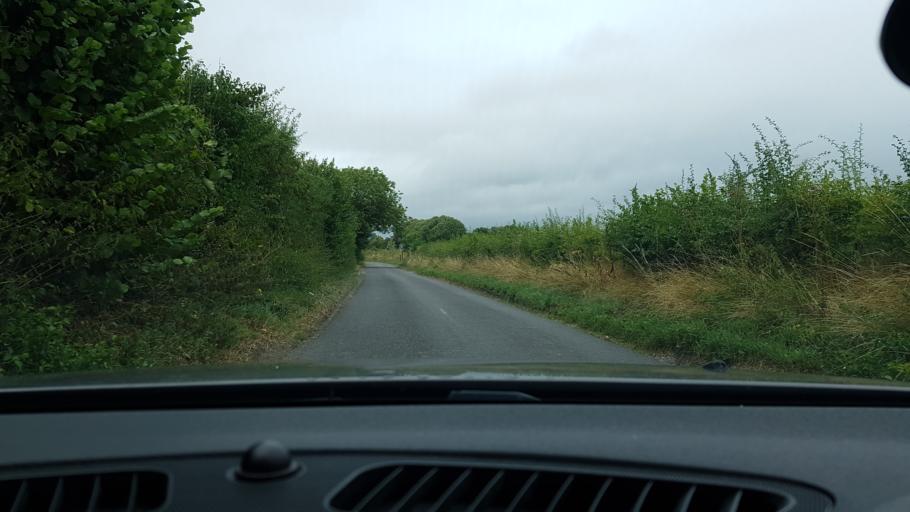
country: GB
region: England
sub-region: Wiltshire
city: Shalbourne
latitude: 51.3579
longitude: -1.5239
